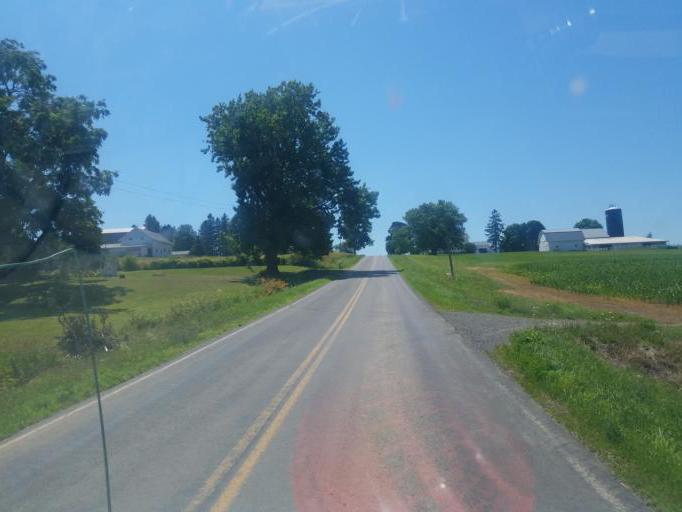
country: US
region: New York
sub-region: Ontario County
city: Geneva
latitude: 42.7990
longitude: -77.0226
